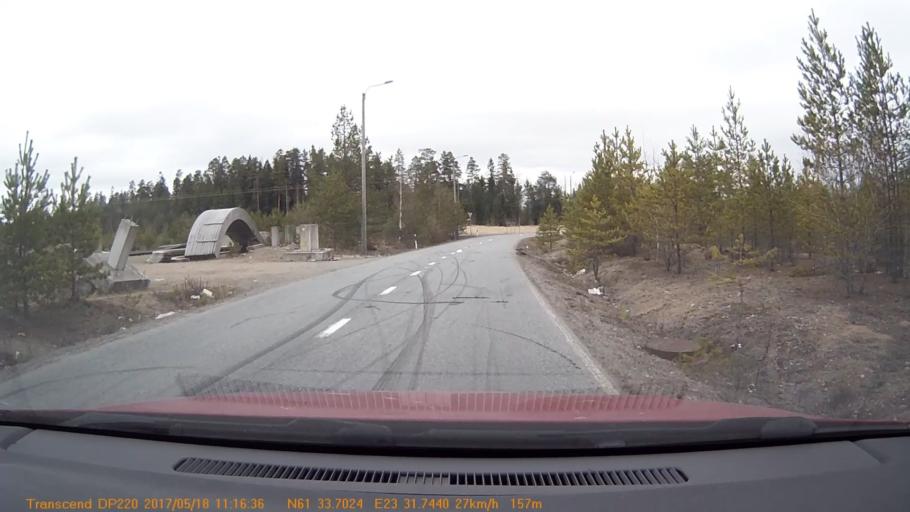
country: FI
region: Pirkanmaa
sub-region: Tampere
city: Yloejaervi
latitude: 61.5617
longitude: 23.5291
